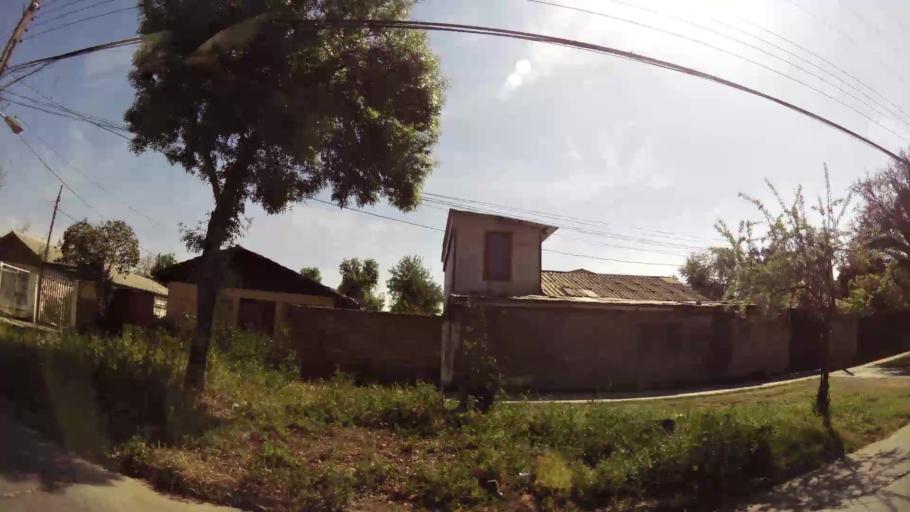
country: CL
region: Santiago Metropolitan
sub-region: Provincia de Santiago
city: Villa Presidente Frei, Nunoa, Santiago, Chile
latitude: -33.4856
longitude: -70.5882
